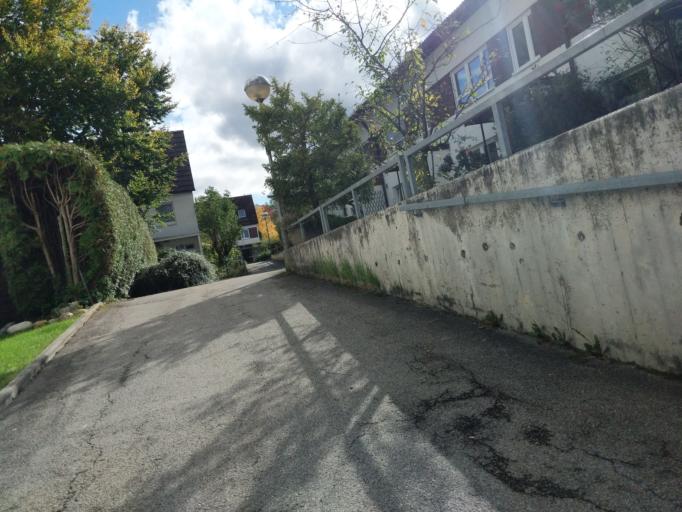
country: DE
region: Bavaria
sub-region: Upper Bavaria
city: Zorneding
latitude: 48.0871
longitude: 11.8351
